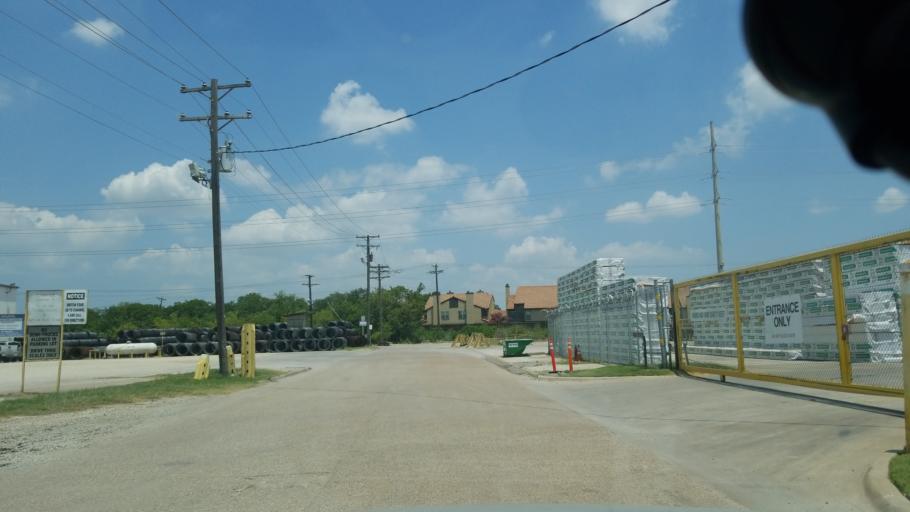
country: US
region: Texas
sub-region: Dallas County
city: Carrollton
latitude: 32.9584
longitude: -96.8641
